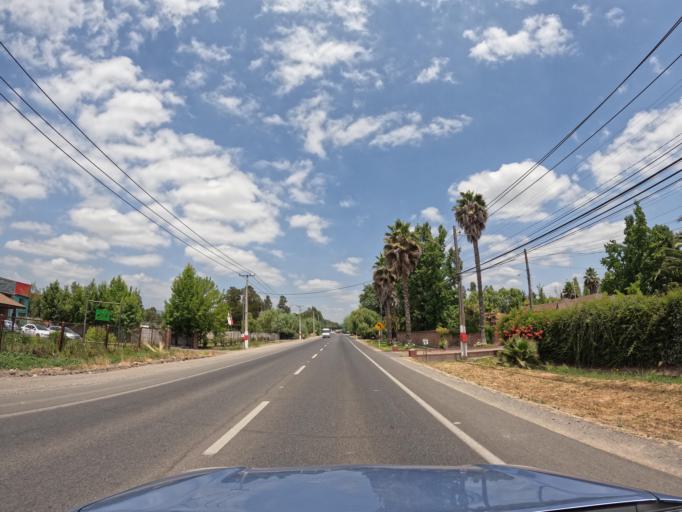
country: CL
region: Maule
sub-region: Provincia de Curico
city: Curico
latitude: -35.0137
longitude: -71.2170
